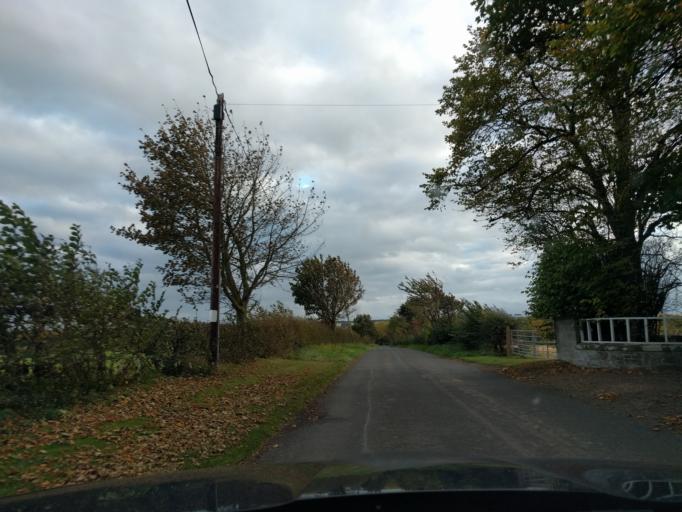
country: GB
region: England
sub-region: Northumberland
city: Ancroft
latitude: 55.7363
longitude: -2.0965
